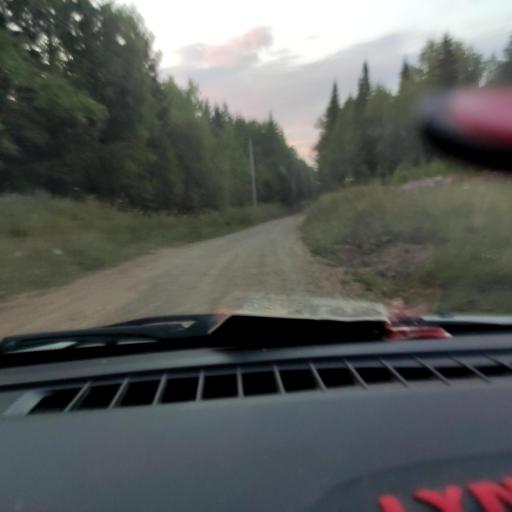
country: RU
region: Perm
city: Kukushtan
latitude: 57.6190
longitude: 56.4745
